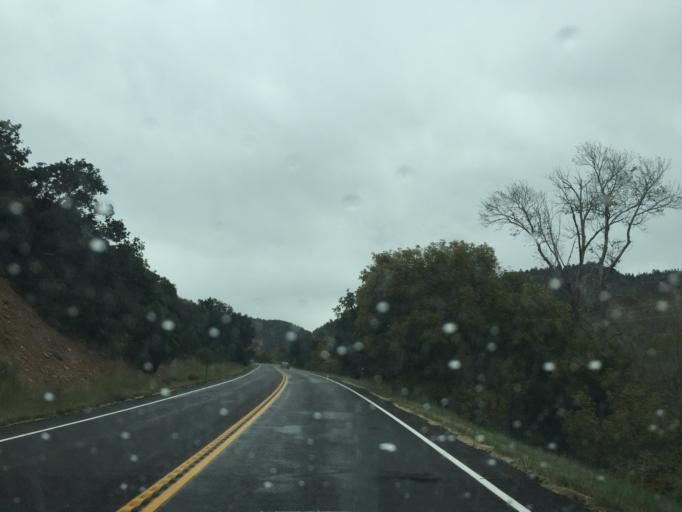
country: US
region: Utah
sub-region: Kane County
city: Kanab
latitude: 37.3504
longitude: -112.5984
